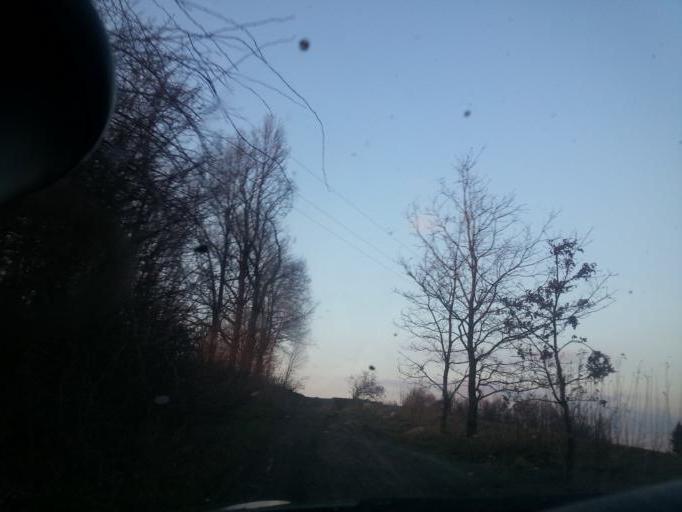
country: PL
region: Lower Silesian Voivodeship
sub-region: Powiat jeleniogorski
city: Stara Kamienica
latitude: 50.9551
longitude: 15.6235
